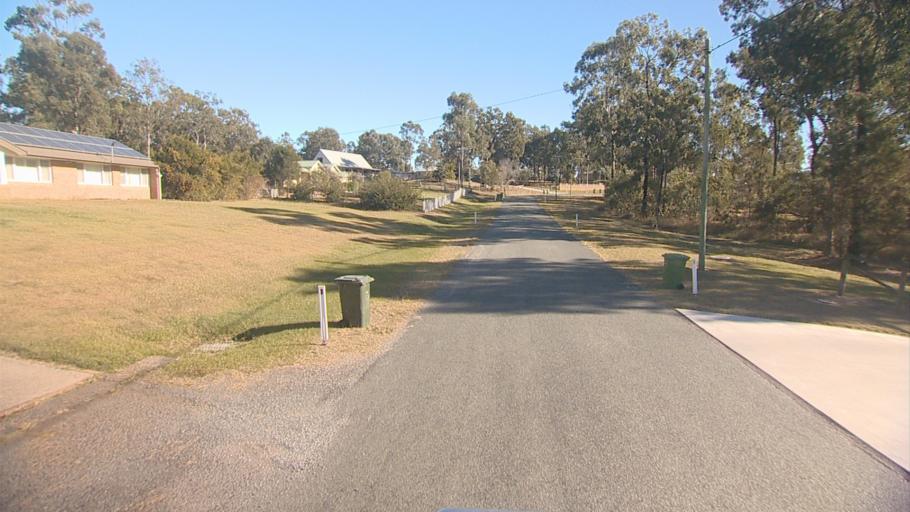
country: AU
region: Queensland
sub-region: Logan
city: North Maclean
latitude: -27.7398
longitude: 152.9648
